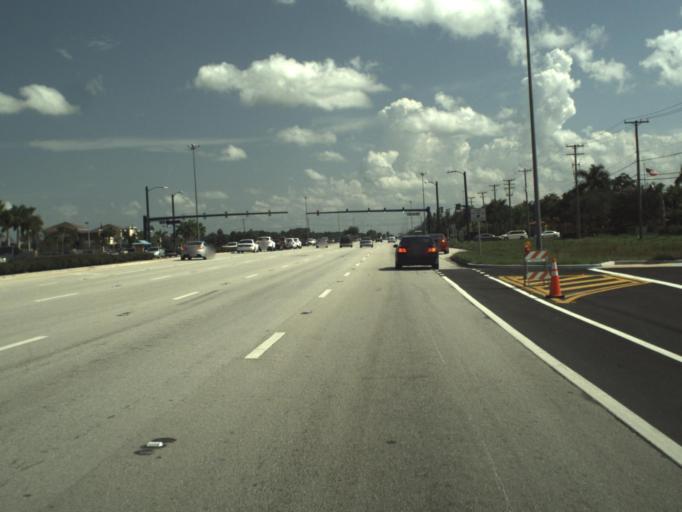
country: US
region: Florida
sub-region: Palm Beach County
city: Wellington
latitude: 26.6667
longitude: -80.2030
